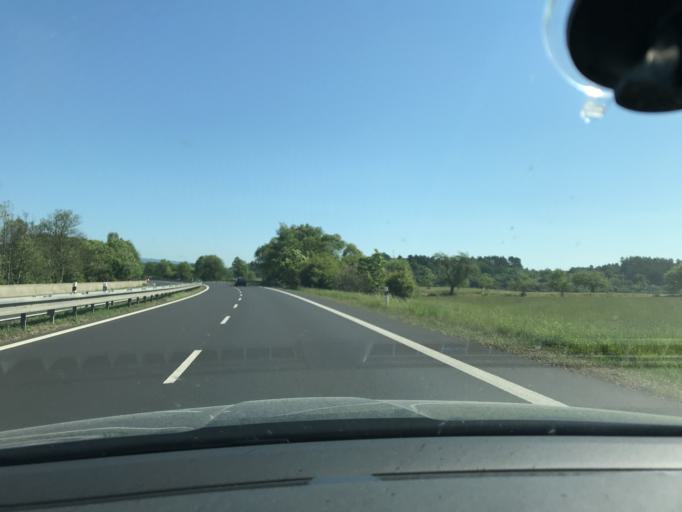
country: CZ
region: Karlovarsky
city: Ostrov
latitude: 50.2728
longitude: 12.9371
